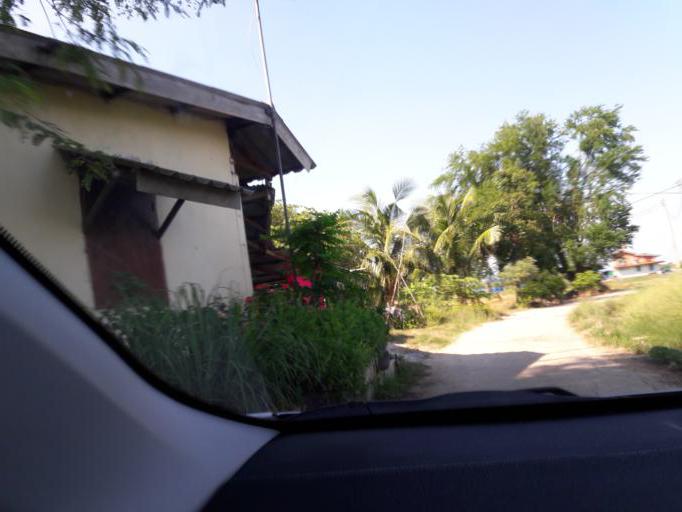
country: TH
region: Ang Thong
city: Ang Thong
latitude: 14.5620
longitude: 100.3947
